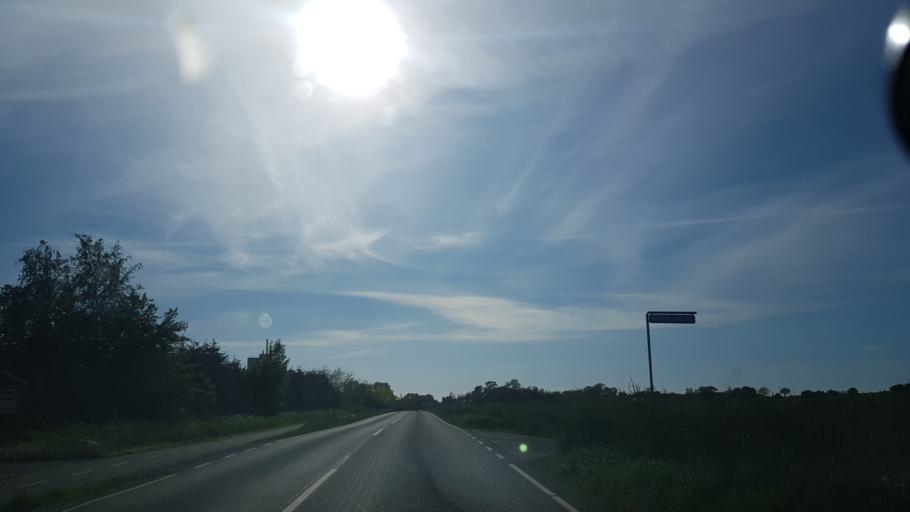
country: DK
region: Zealand
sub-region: Slagelse Kommune
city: Forlev
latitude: 55.4367
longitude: 11.2632
